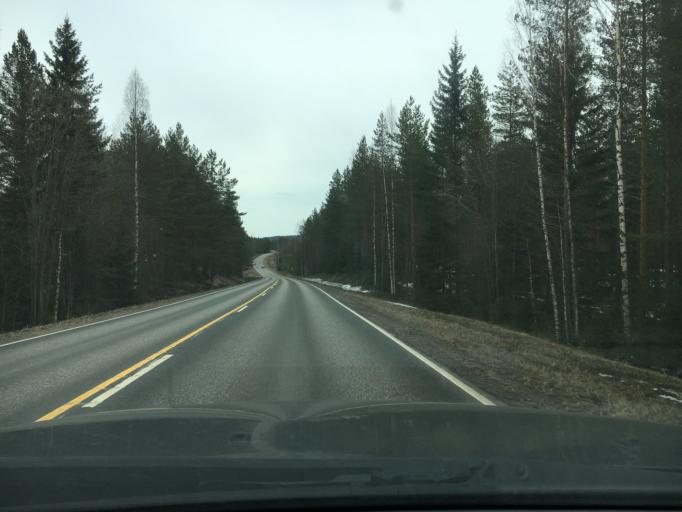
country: FI
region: Central Finland
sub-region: AEaenekoski
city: Sumiainen
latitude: 62.5572
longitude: 26.0316
